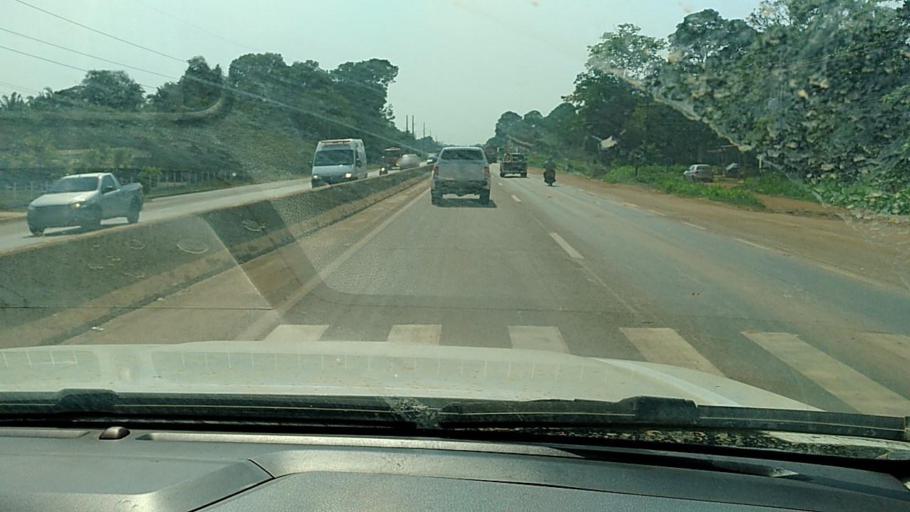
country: BR
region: Rondonia
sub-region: Porto Velho
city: Porto Velho
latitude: -8.7998
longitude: -63.7794
